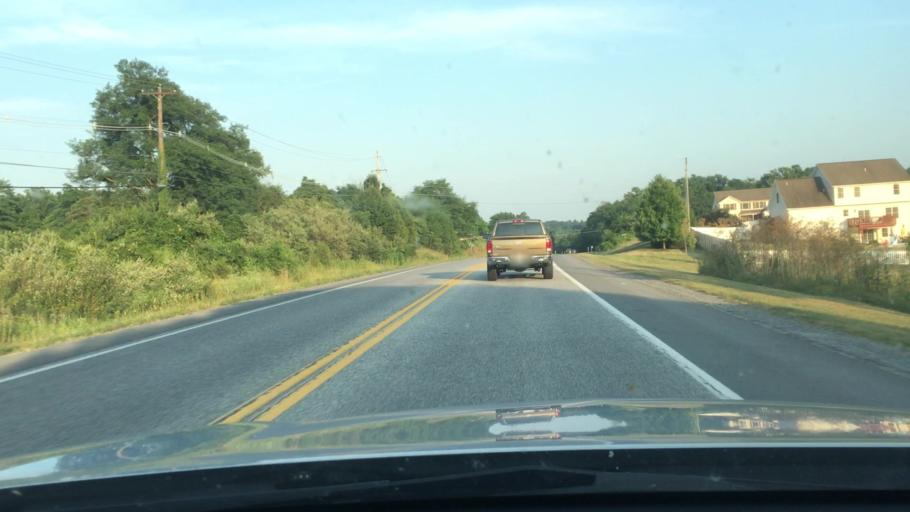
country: US
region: Pennsylvania
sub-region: York County
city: Dillsburg
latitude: 40.0868
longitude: -76.9450
